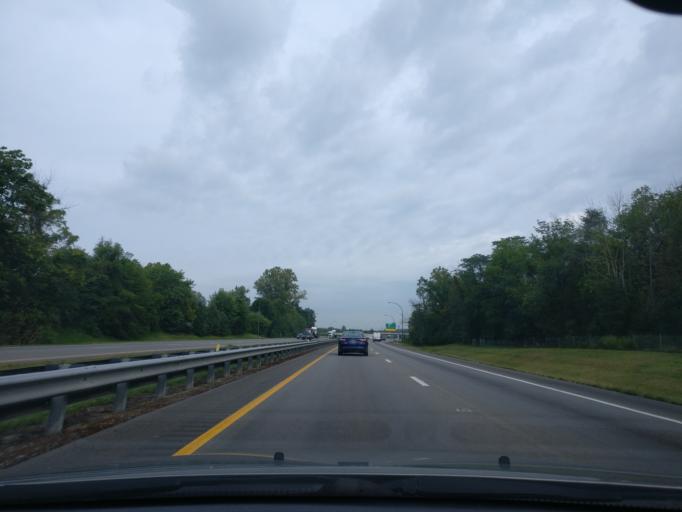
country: US
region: Ohio
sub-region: Greene County
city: Beavercreek
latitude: 39.7171
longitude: -84.0529
